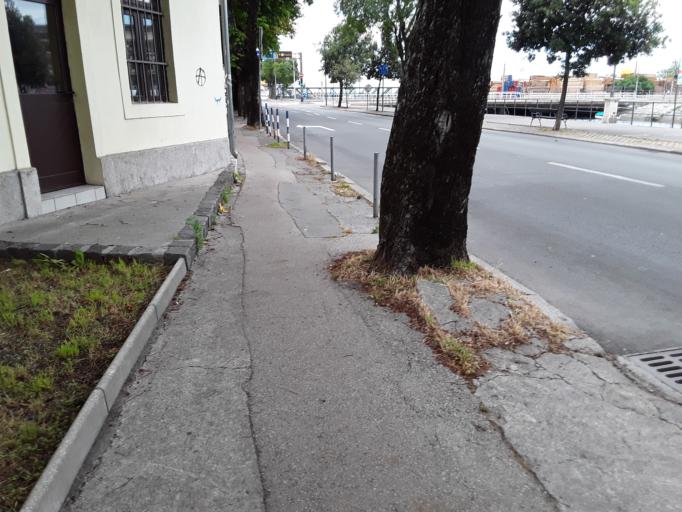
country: HR
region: Primorsko-Goranska
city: Drenova
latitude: 45.3244
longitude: 14.4492
